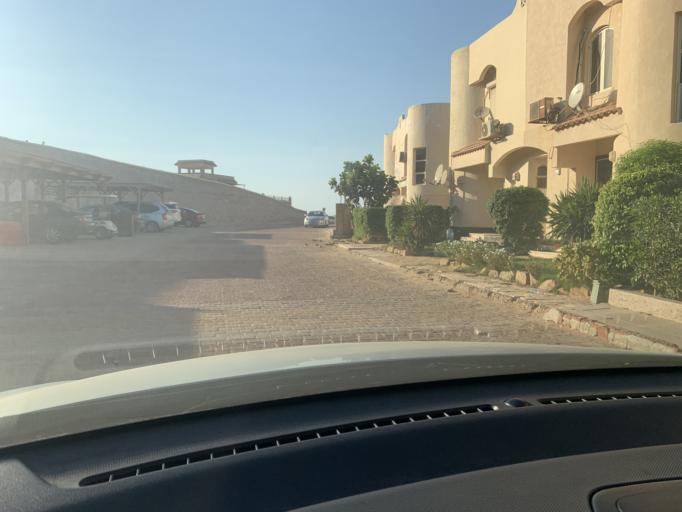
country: EG
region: As Suways
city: Ain Sukhna
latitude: 29.3751
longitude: 32.5706
